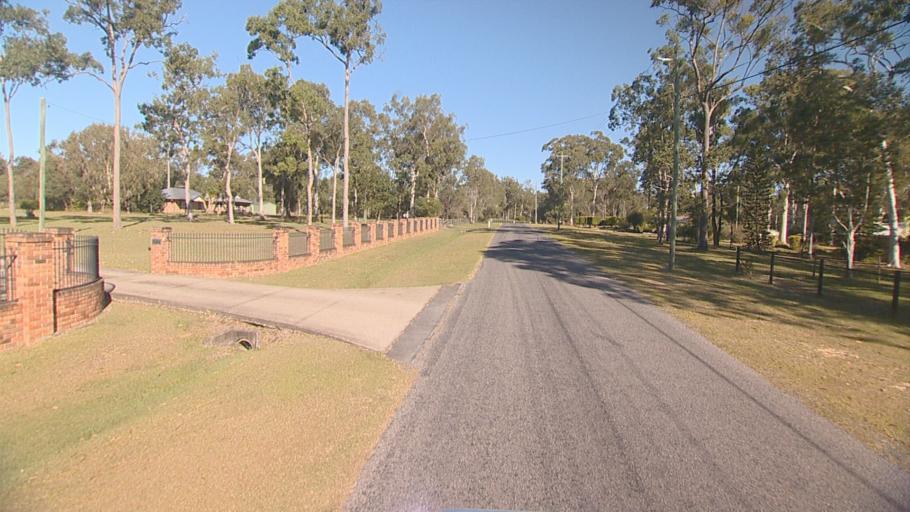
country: AU
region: Queensland
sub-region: Logan
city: Chambers Flat
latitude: -27.7379
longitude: 153.0708
